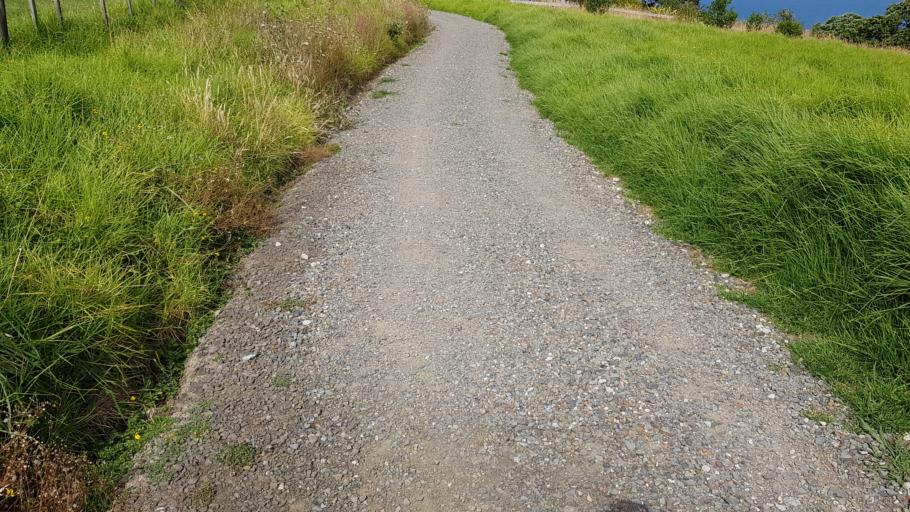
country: NZ
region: Auckland
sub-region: Auckland
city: Rothesay Bay
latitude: -36.6716
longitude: 174.7465
